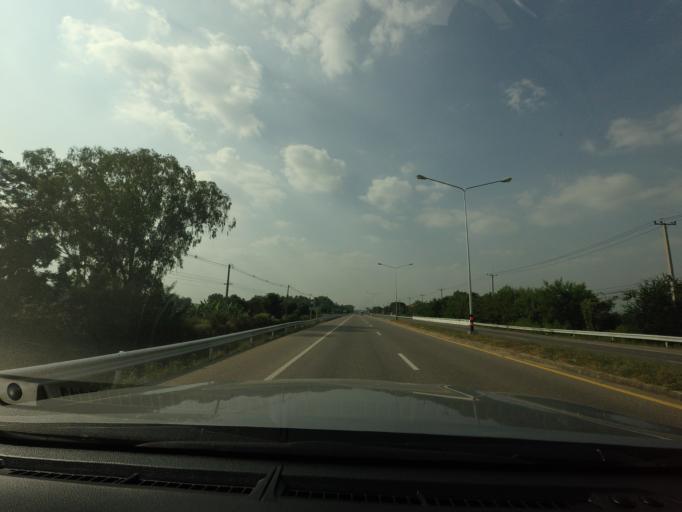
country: TH
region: Sukhothai
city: Sukhothai
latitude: 17.0195
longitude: 99.9020
